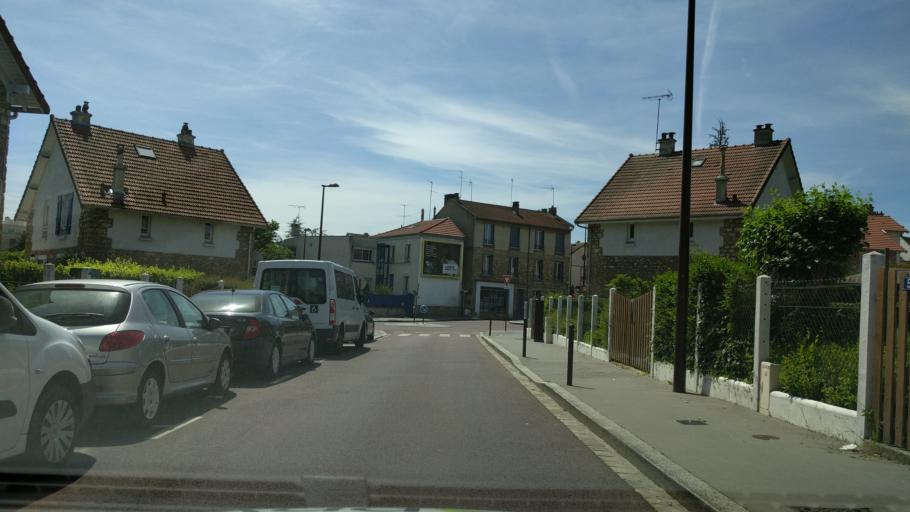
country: FR
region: Ile-de-France
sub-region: Departement des Yvelines
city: Viroflay
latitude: 48.8070
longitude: 2.1601
